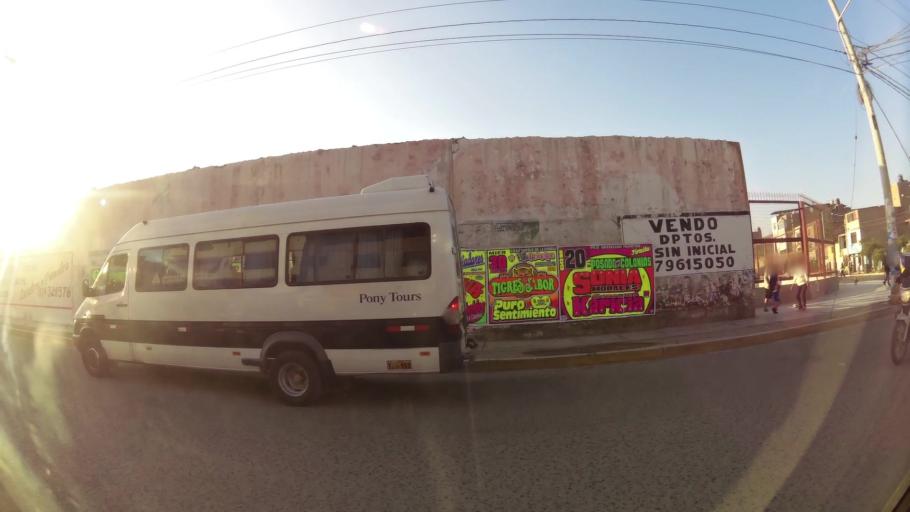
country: PE
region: Lambayeque
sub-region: Provincia de Chiclayo
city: Santa Rosa
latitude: -6.7748
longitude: -79.8324
